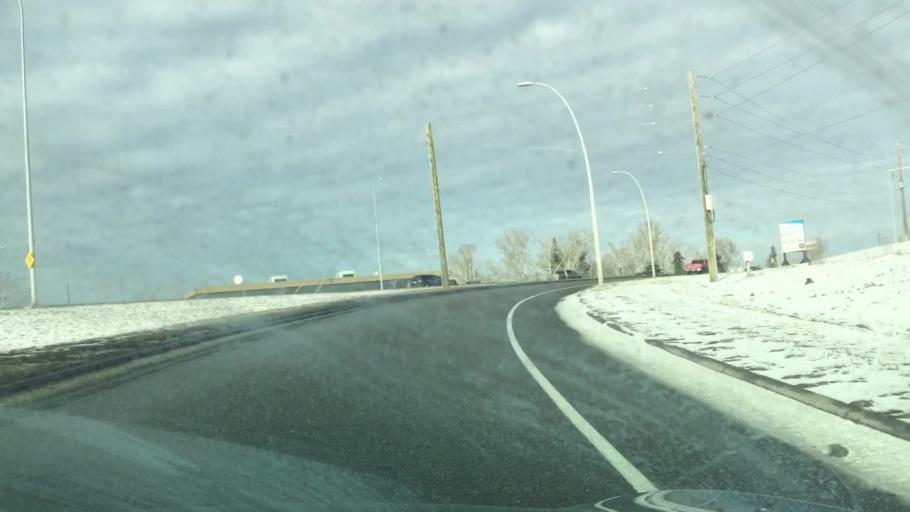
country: CA
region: Alberta
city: Calgary
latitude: 50.9960
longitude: -114.0501
